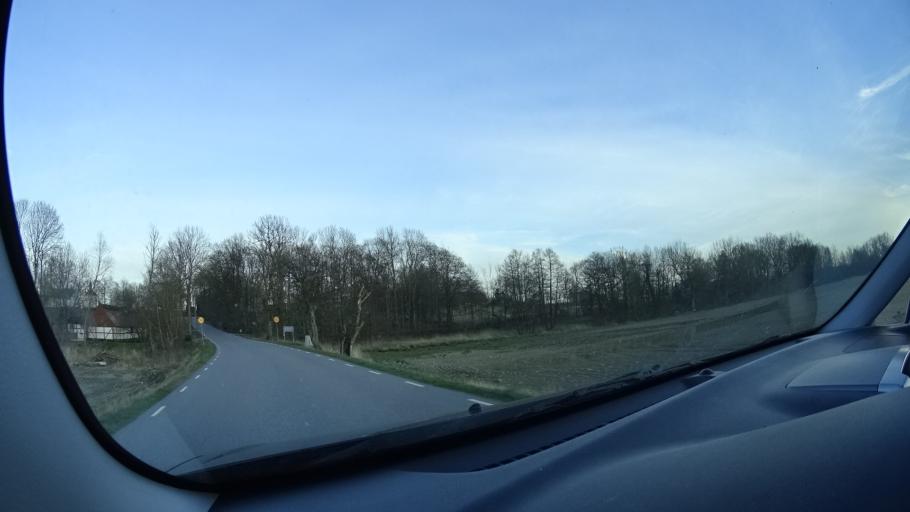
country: SE
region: Skane
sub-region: Eslovs Kommun
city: Stehag
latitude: 55.8978
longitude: 13.4120
